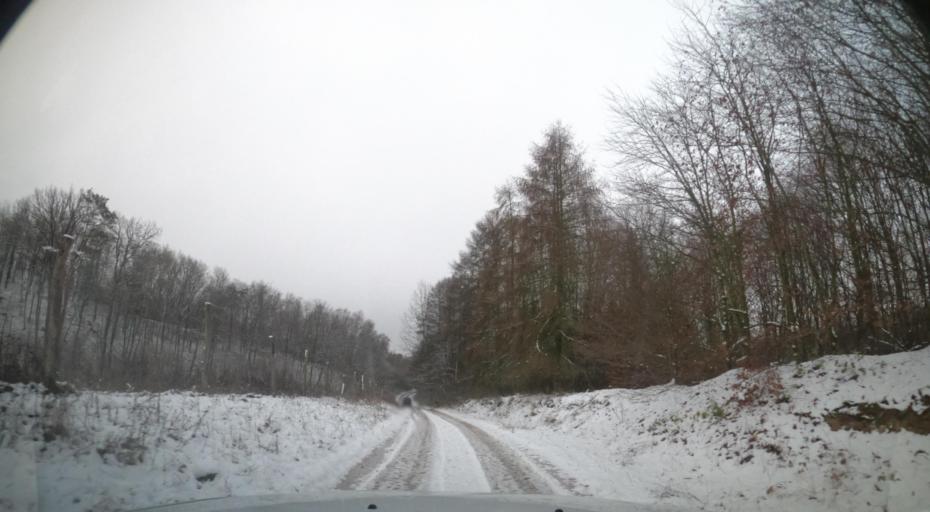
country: PL
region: West Pomeranian Voivodeship
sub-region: Powiat mysliborski
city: Barlinek
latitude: 53.0665
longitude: 15.1903
